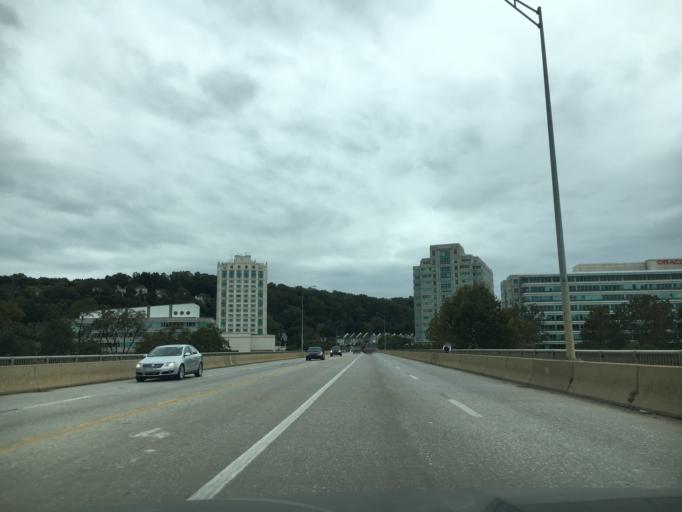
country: US
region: Pennsylvania
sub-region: Montgomery County
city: West Conshohocken
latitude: 40.0718
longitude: -75.3084
